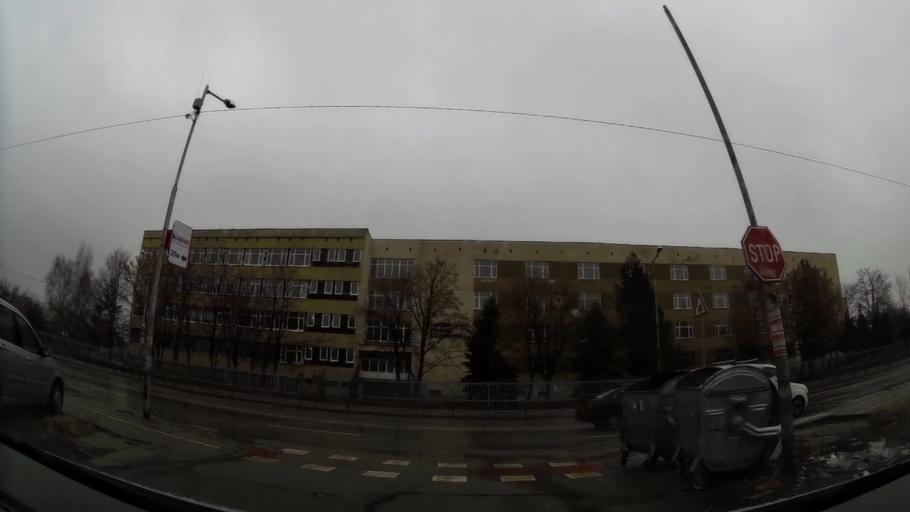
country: BG
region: Sofia-Capital
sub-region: Stolichna Obshtina
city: Sofia
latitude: 42.6343
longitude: 23.3801
